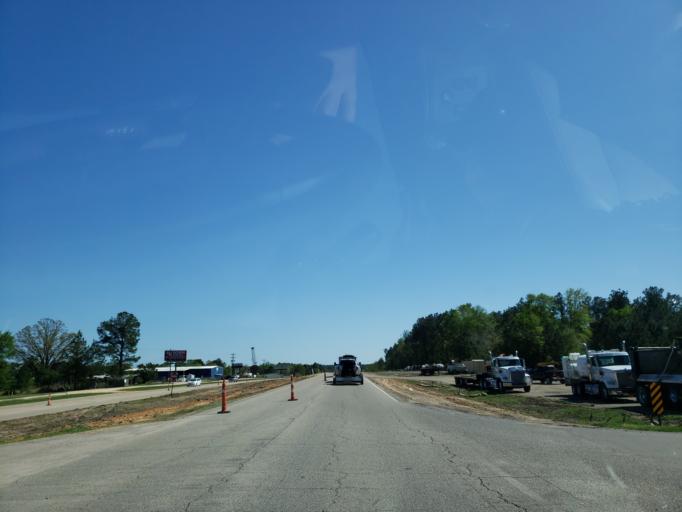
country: US
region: Mississippi
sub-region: Lamar County
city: Purvis
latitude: 31.0705
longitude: -89.2094
